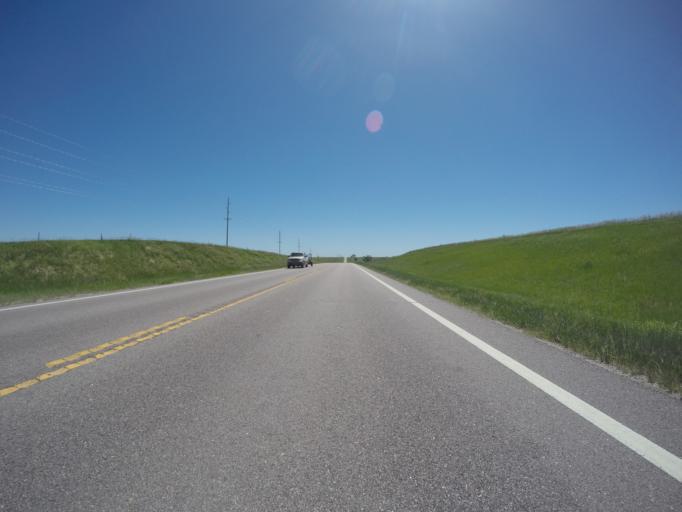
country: US
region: Kansas
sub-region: Norton County
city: Norton
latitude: 39.8284
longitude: -99.6738
